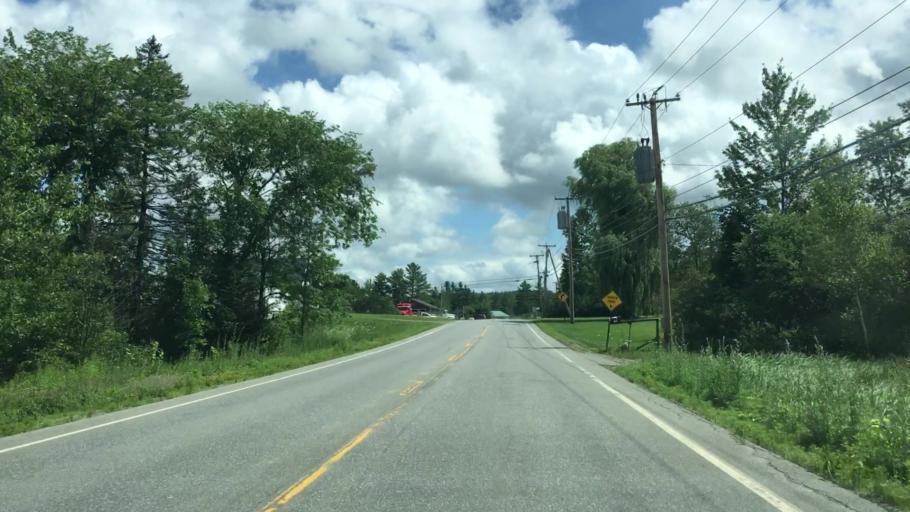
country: US
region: Maine
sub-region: Penobscot County
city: Hermon
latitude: 44.8087
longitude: -68.9821
